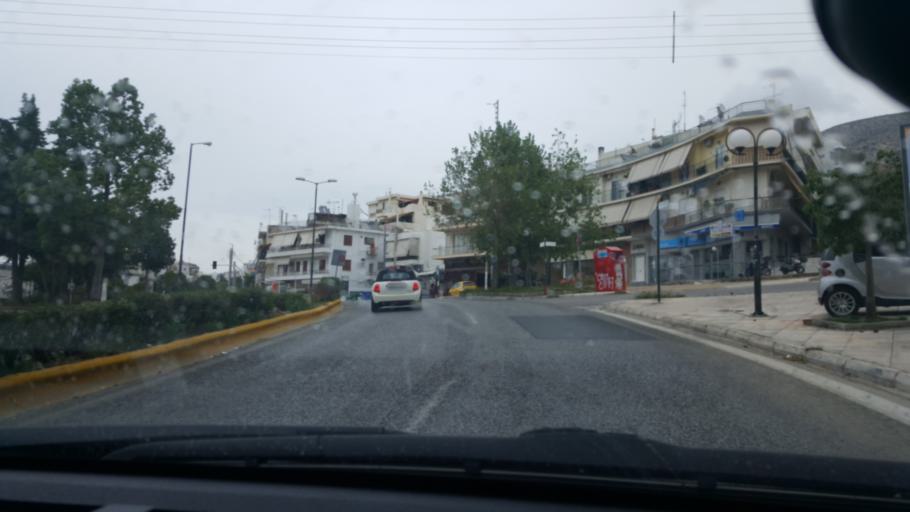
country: GR
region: Attica
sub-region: Nomarchia Athinas
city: Ilioupoli
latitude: 37.9285
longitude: 23.7590
